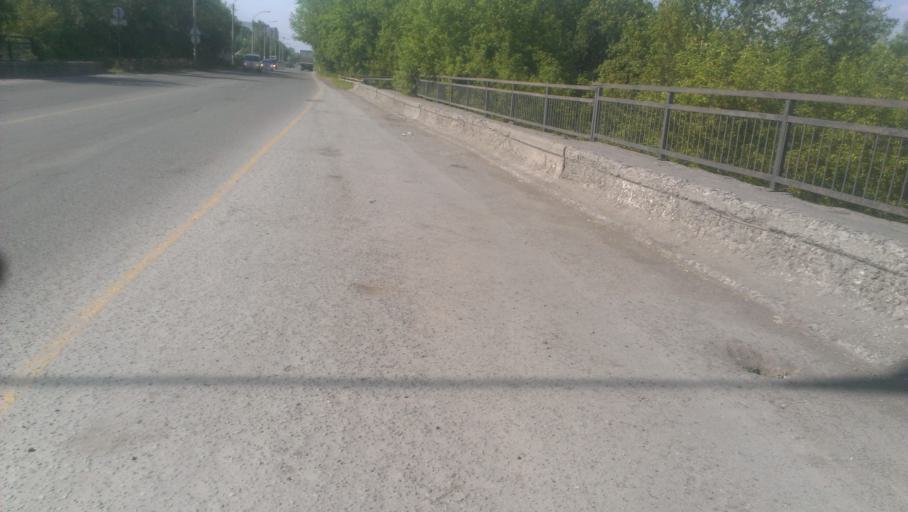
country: RU
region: Altai Krai
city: Novoaltaysk
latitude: 53.4045
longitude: 83.9452
